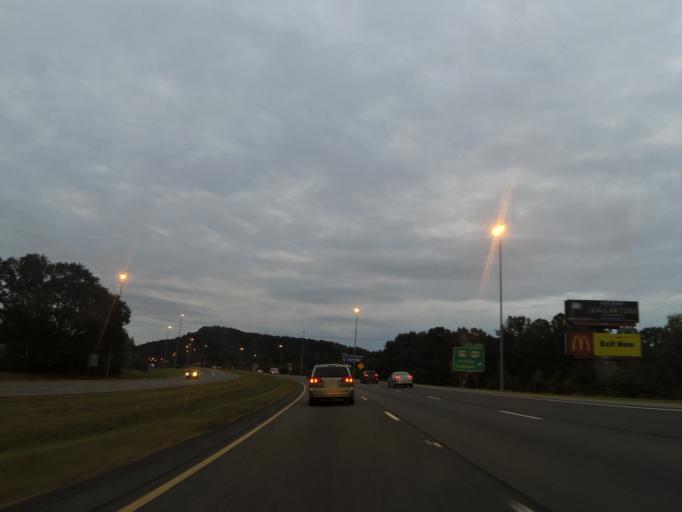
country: US
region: Alabama
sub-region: Etowah County
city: Attalla
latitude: 34.0131
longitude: -86.0746
